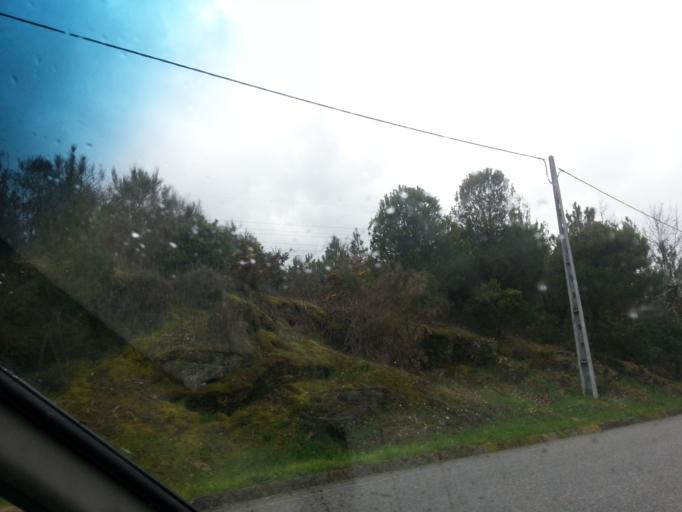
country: PT
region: Viseu
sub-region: Viseu
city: Rio de Loba
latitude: 40.6055
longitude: -7.8503
